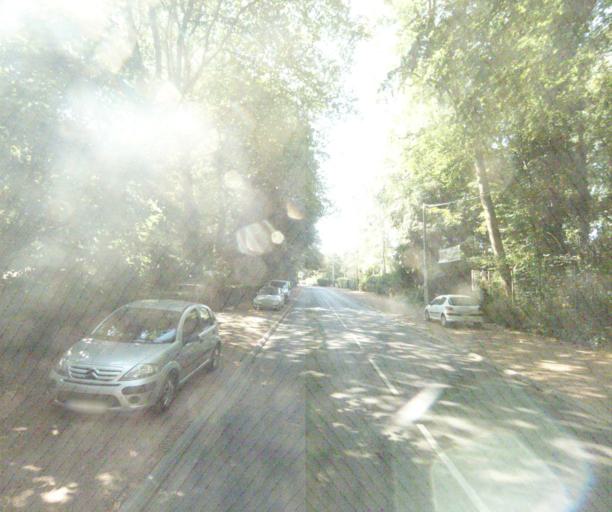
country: FR
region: Nord-Pas-de-Calais
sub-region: Departement du Nord
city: Wervicq-Sud
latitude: 50.7646
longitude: 3.0476
